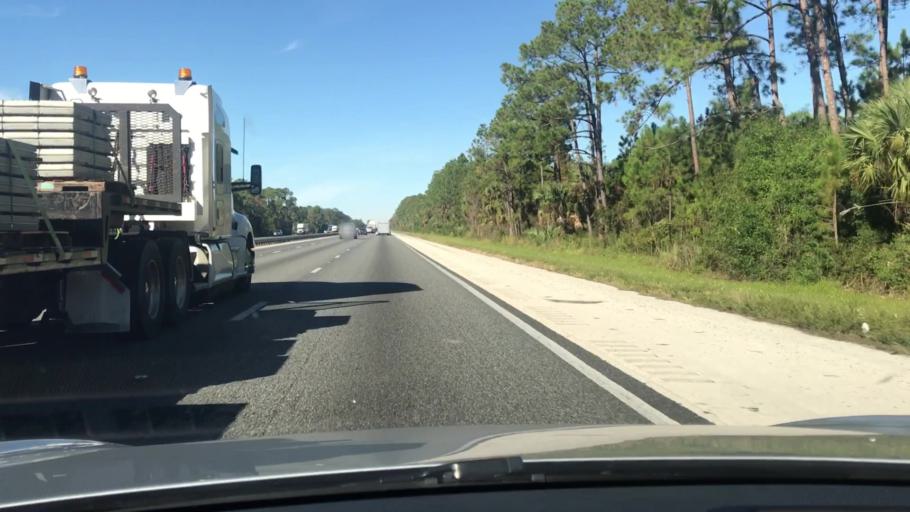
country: US
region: Florida
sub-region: Volusia County
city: Ormond-by-the-Sea
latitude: 29.3631
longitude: -81.1374
